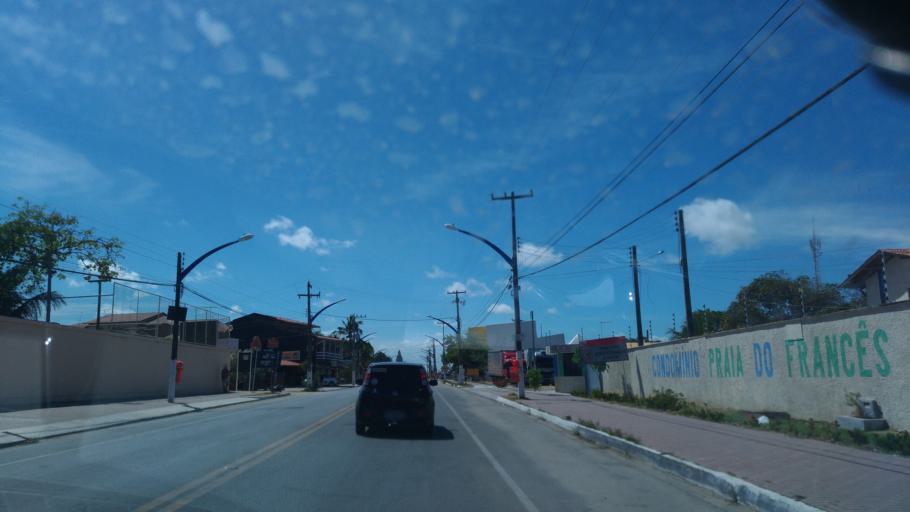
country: BR
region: Alagoas
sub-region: Marechal Deodoro
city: Marechal Deodoro
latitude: -9.7695
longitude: -35.8450
